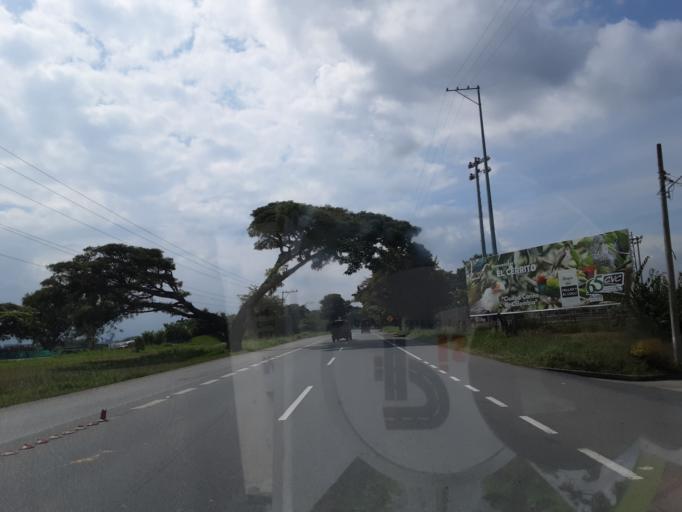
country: CO
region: Valle del Cauca
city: El Cerrito
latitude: 3.6877
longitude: -76.3085
